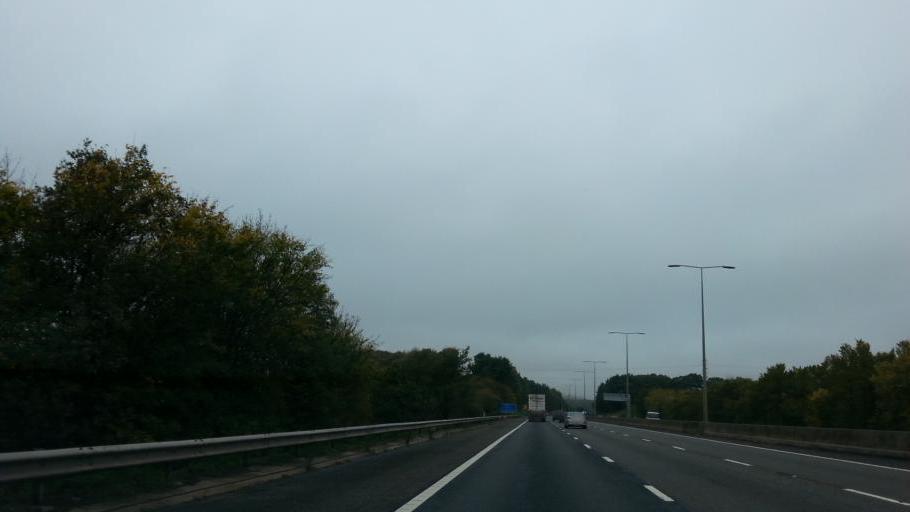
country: GB
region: England
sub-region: Worcestershire
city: Barnt Green
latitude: 52.3896
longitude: -2.0510
